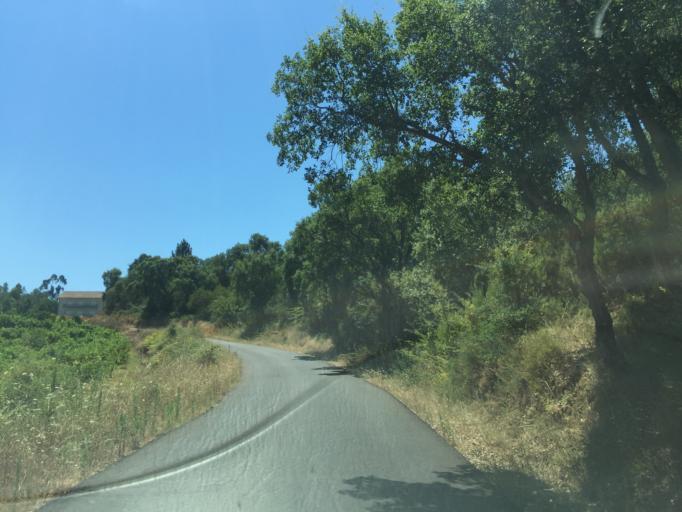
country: PT
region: Santarem
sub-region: Ferreira do Zezere
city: Ferreira do Zezere
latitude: 39.5964
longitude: -8.2716
